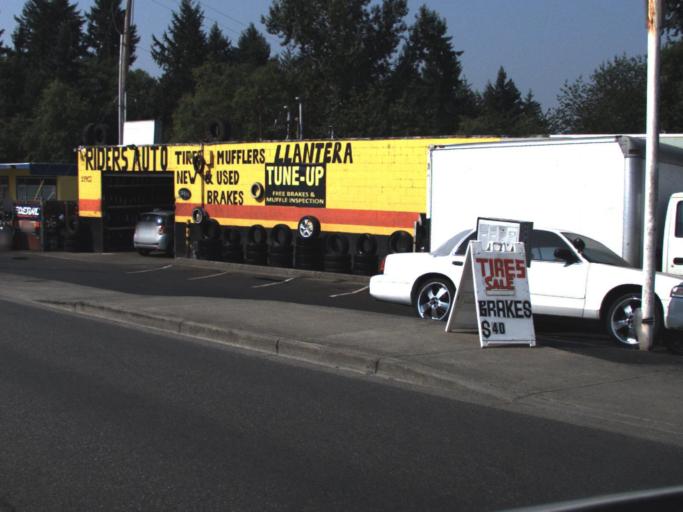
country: US
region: Washington
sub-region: King County
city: Des Moines
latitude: 47.3816
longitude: -122.2978
